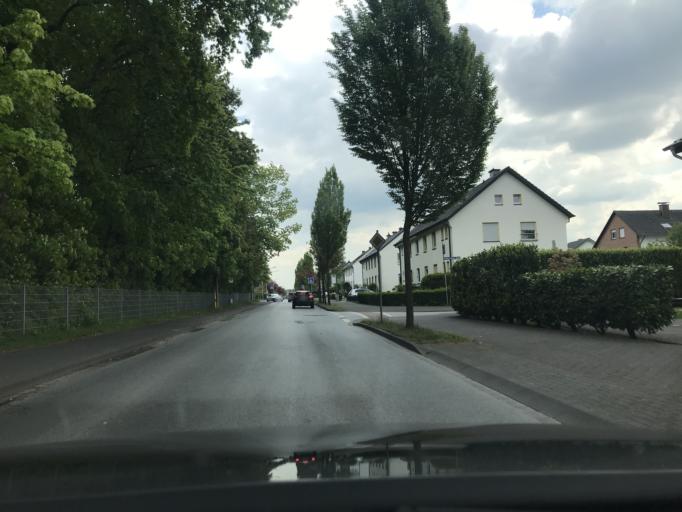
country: DE
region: North Rhine-Westphalia
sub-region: Regierungsbezirk Detmold
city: Rheda-Wiedenbruck
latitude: 51.8532
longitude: 8.2774
